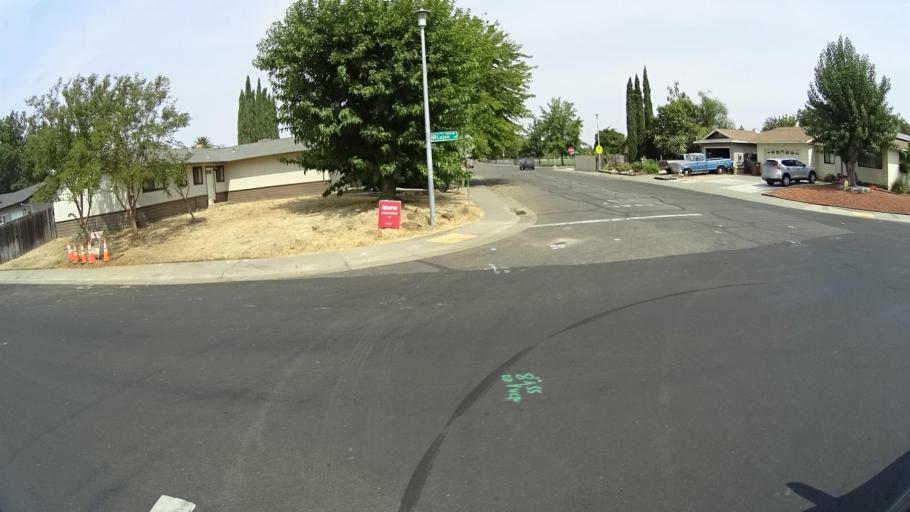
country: US
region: California
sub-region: Sacramento County
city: Elk Grove
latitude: 38.4187
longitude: -121.3792
